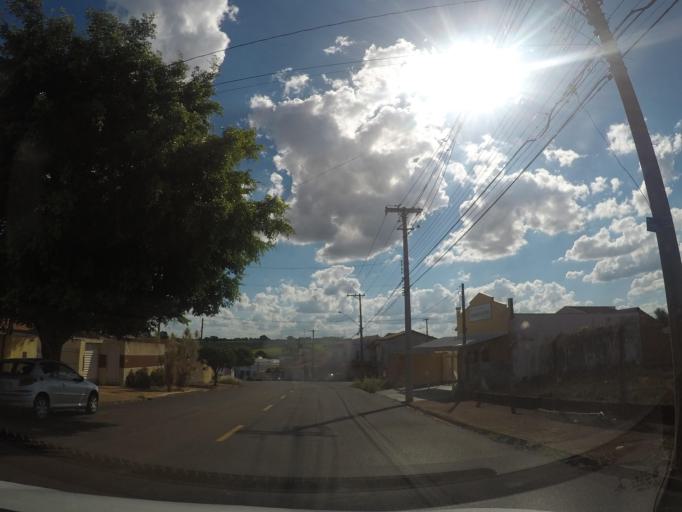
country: BR
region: Sao Paulo
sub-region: Sumare
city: Sumare
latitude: -22.8317
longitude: -47.2797
